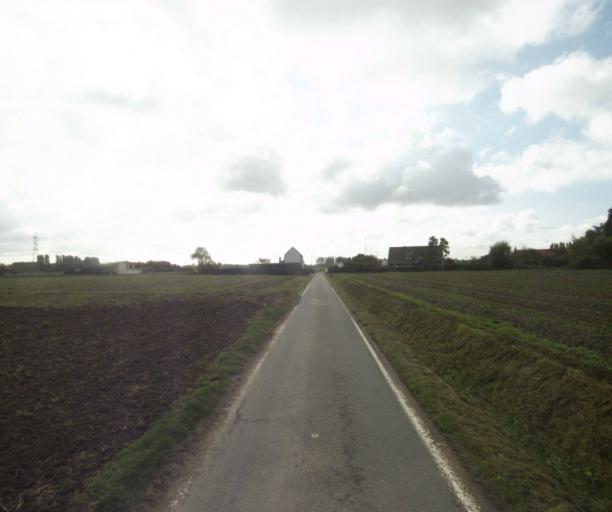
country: FR
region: Nord-Pas-de-Calais
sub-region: Departement du Nord
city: Verlinghem
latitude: 50.6735
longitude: 3.0102
